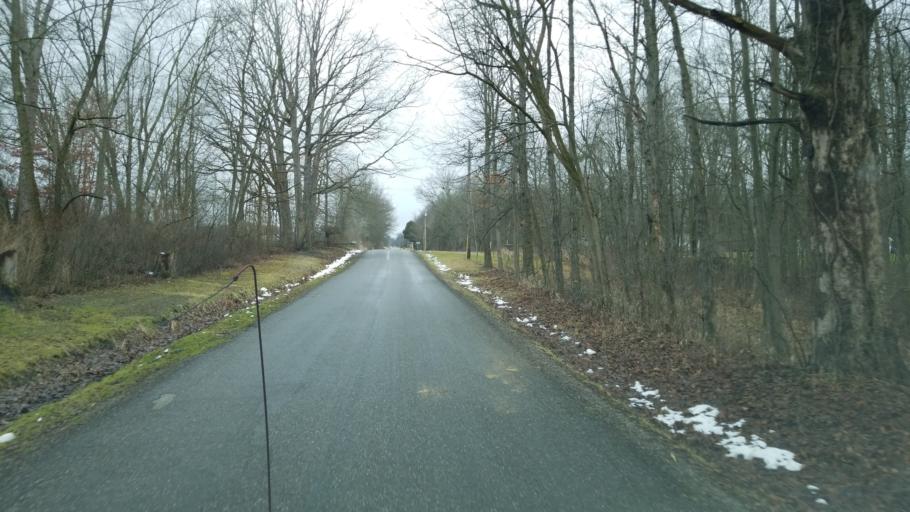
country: US
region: Ohio
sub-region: Trumbull County
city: Leavittsburg
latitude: 41.3393
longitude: -80.9629
